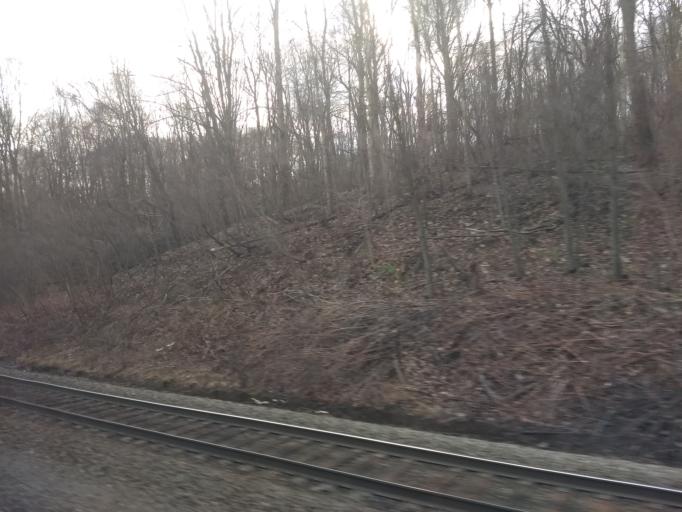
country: US
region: Pennsylvania
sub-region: Cambria County
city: Vinco
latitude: 40.3763
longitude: -78.8522
